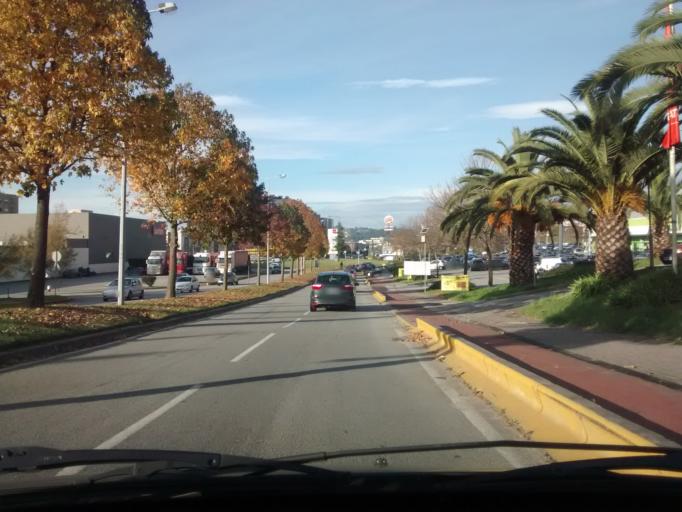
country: PT
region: Braga
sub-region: Braga
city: Braga
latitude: 41.5405
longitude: -8.3986
